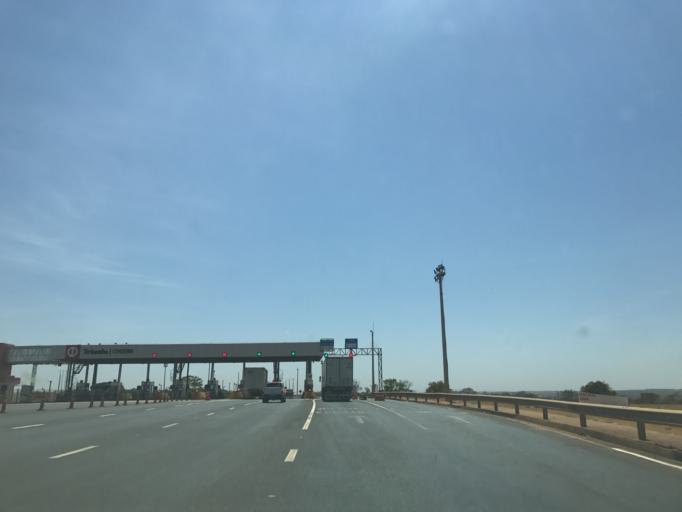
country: BR
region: Minas Gerais
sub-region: Prata
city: Prata
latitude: -19.4723
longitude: -48.8704
